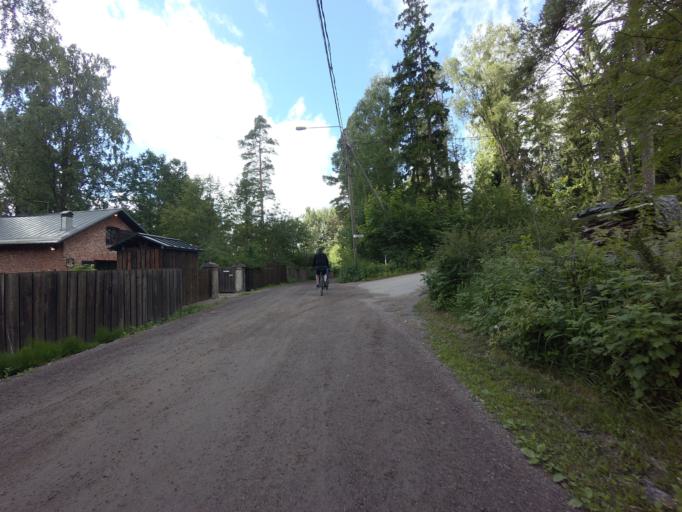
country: FI
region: Uusimaa
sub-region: Helsinki
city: Espoo
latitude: 60.1640
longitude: 24.5959
